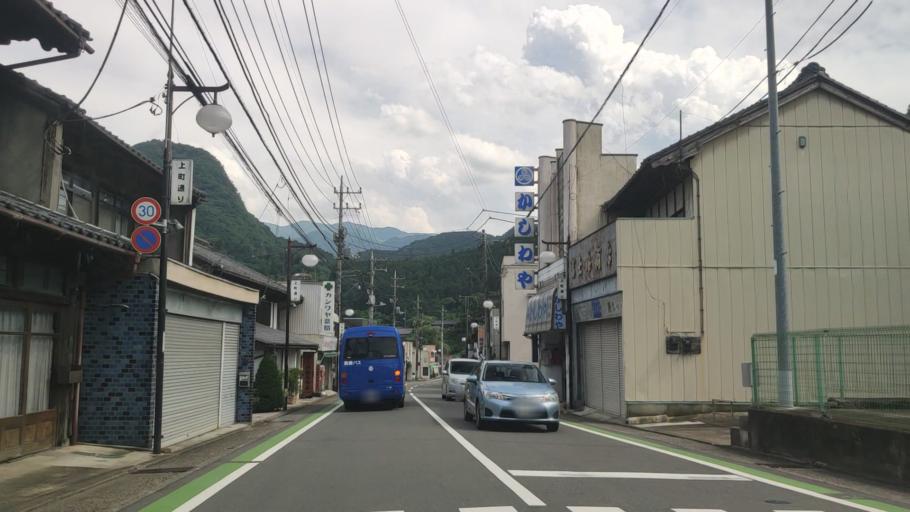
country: JP
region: Gunma
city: Tomioka
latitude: 36.2101
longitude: 138.7828
